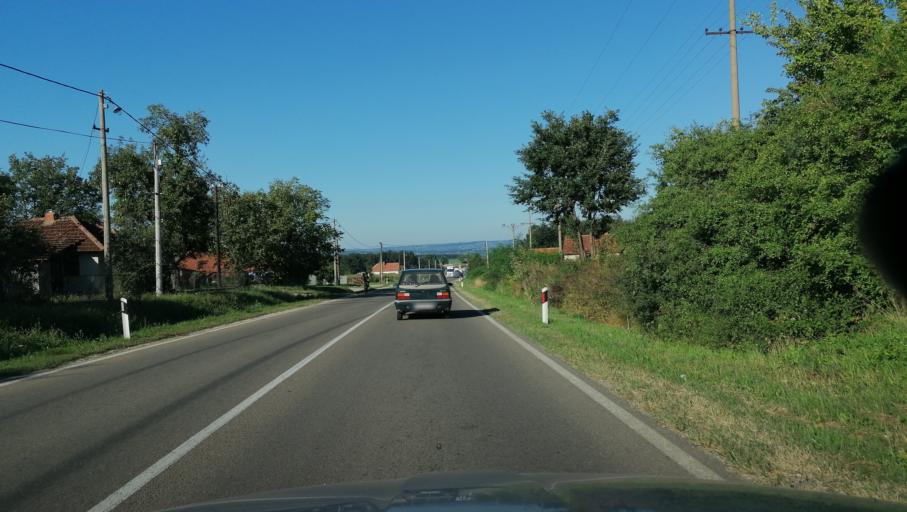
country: RS
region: Central Serbia
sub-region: Sumadijski Okrug
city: Knic
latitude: 43.9090
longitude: 20.6370
